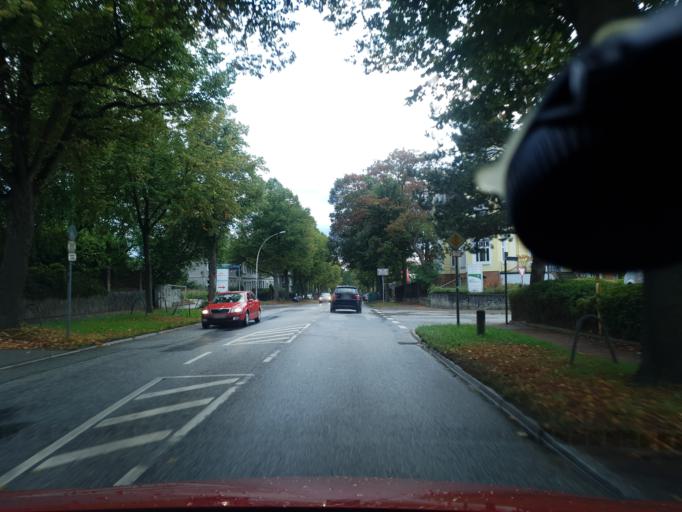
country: DE
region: Schleswig-Holstein
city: Kiel
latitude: 54.2988
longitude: 10.1061
